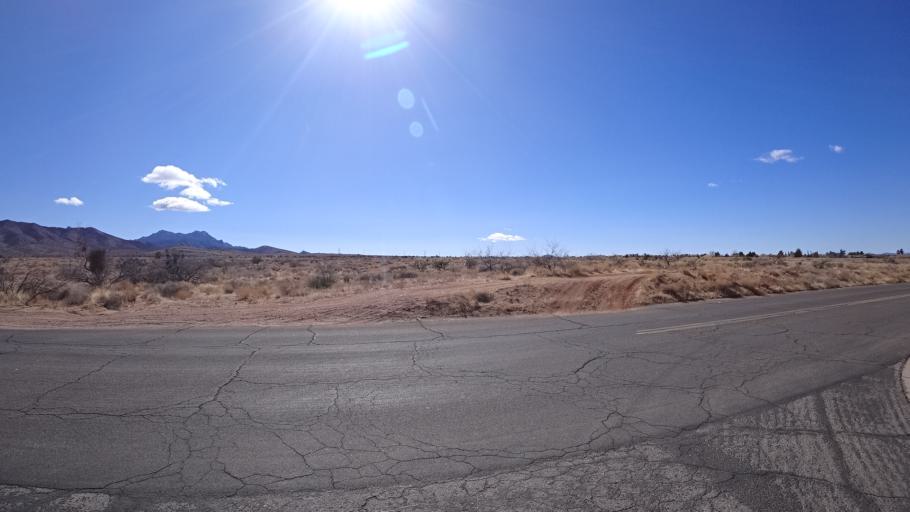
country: US
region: Arizona
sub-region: Mohave County
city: Kingman
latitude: 35.1960
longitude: -113.9715
